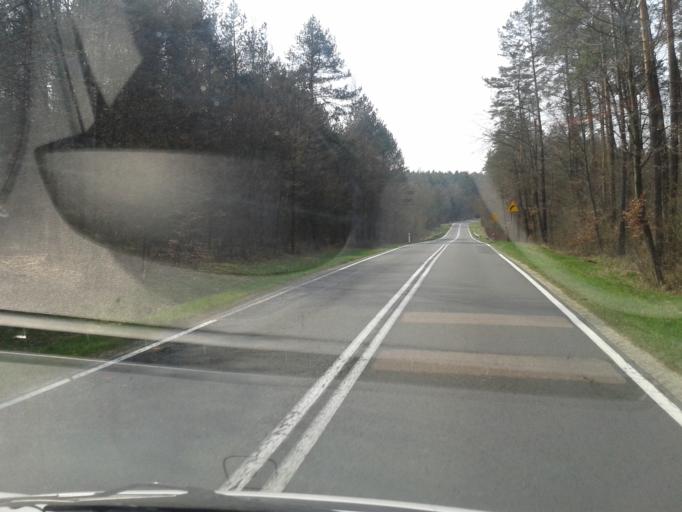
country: PL
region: Subcarpathian Voivodeship
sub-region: Powiat lubaczowski
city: Narol
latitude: 50.3352
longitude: 23.2940
